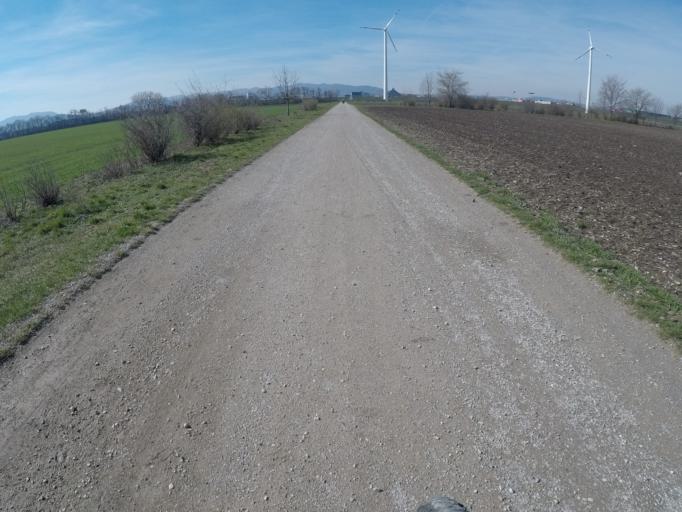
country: AT
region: Lower Austria
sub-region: Politischer Bezirk Modling
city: Vosendorf
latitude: 48.1086
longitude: 16.3292
